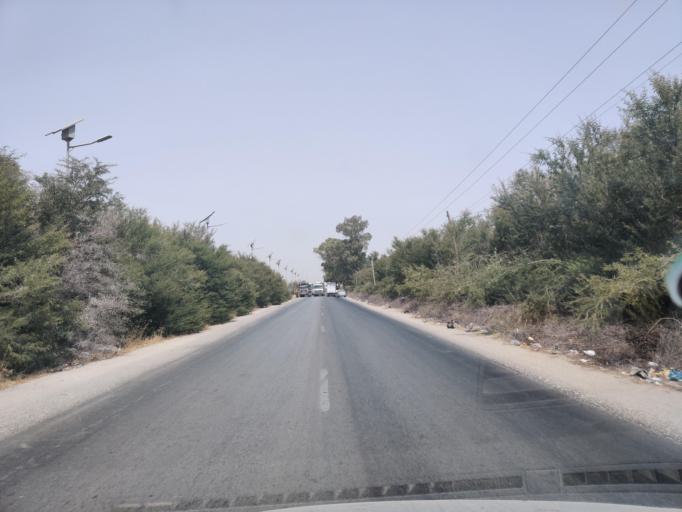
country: TN
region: Tunis
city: La Sebala du Mornag
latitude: 36.6558
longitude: 10.3325
